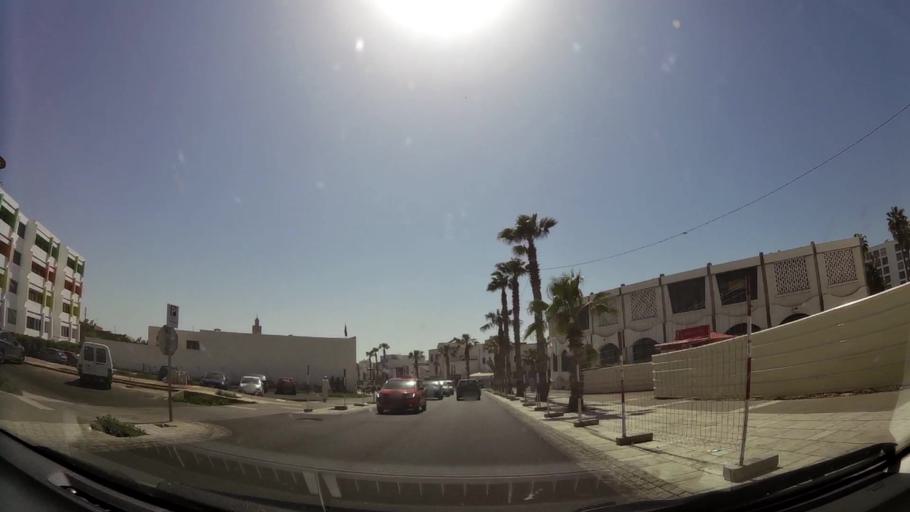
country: MA
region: Souss-Massa-Draa
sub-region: Agadir-Ida-ou-Tnan
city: Agadir
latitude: 30.4243
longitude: -9.5905
